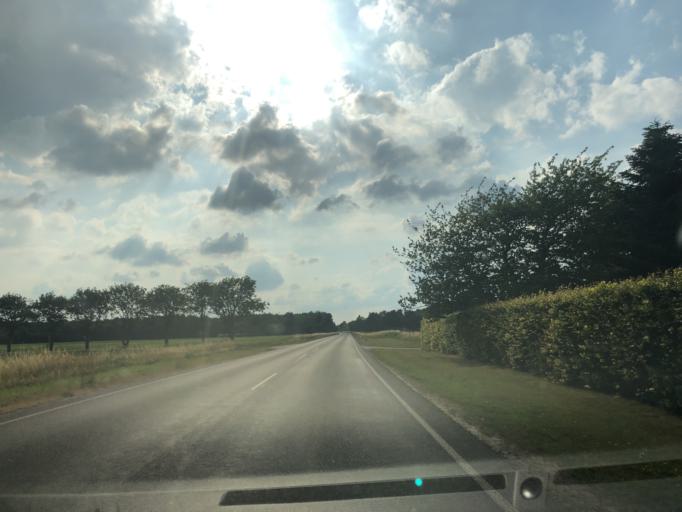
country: DK
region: Zealand
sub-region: Faxe Kommune
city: Fakse
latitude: 55.3131
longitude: 12.1164
